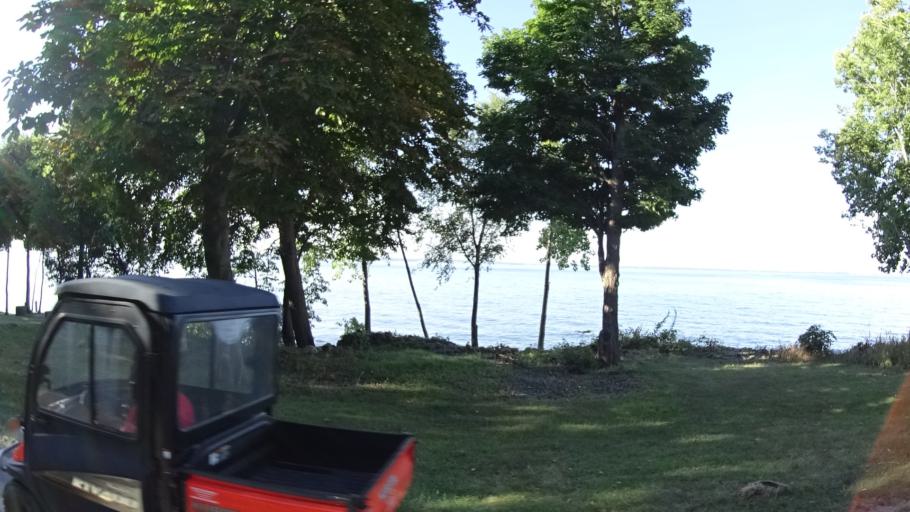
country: US
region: Ohio
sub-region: Erie County
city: Sandusky
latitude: 41.6005
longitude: -82.7332
